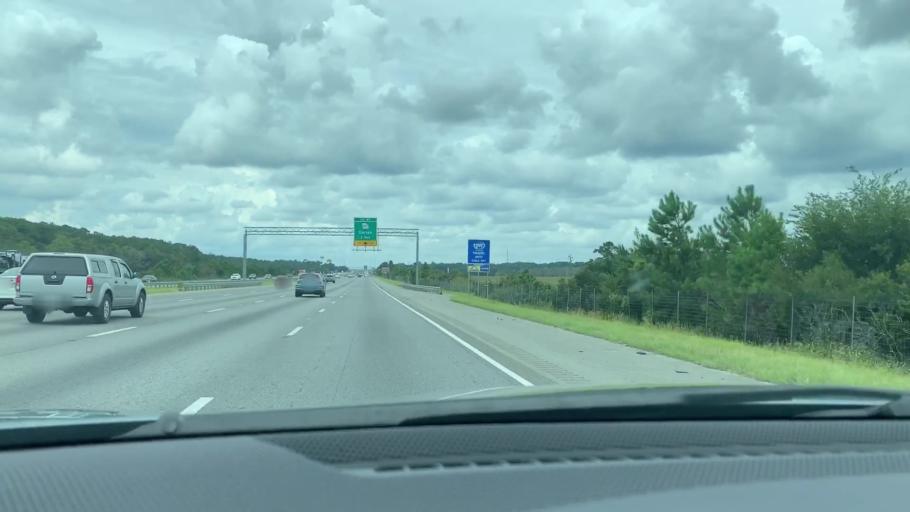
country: US
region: Georgia
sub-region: McIntosh County
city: Darien
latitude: 31.3765
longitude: -81.4539
